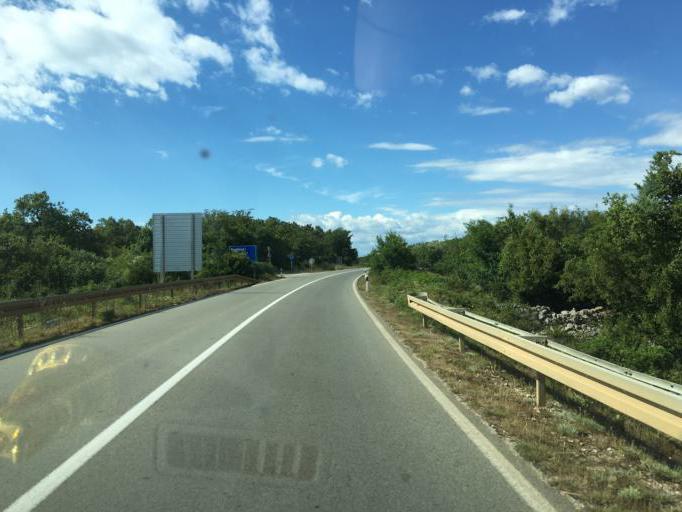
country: HR
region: Primorsko-Goranska
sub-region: Grad Krk
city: Krk
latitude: 45.0444
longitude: 14.5683
